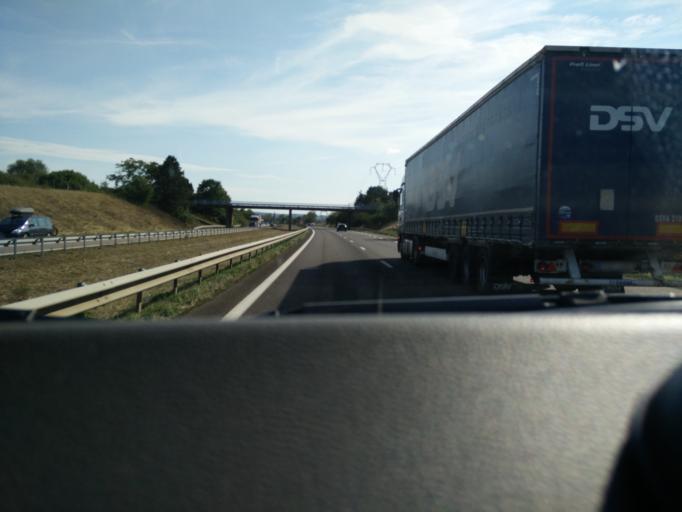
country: FR
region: Lorraine
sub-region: Departement de Meurthe-et-Moselle
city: Pont-a-Mousson
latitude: 48.8869
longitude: 6.0979
